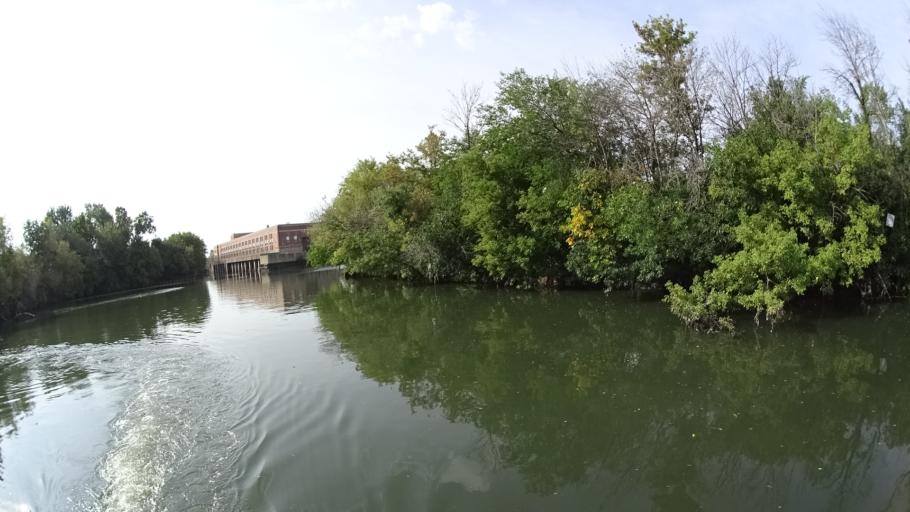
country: US
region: Illinois
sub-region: Cook County
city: Chicago
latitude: 41.8268
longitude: -87.6576
